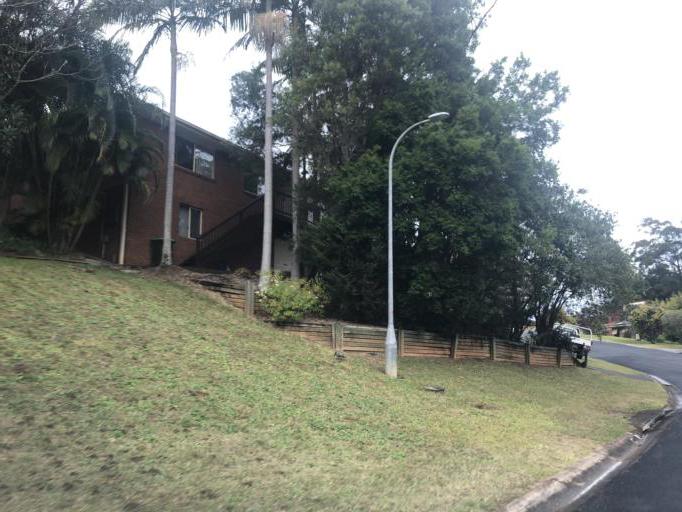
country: AU
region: New South Wales
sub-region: Coffs Harbour
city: Coffs Harbour
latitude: -30.2771
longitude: 153.1095
